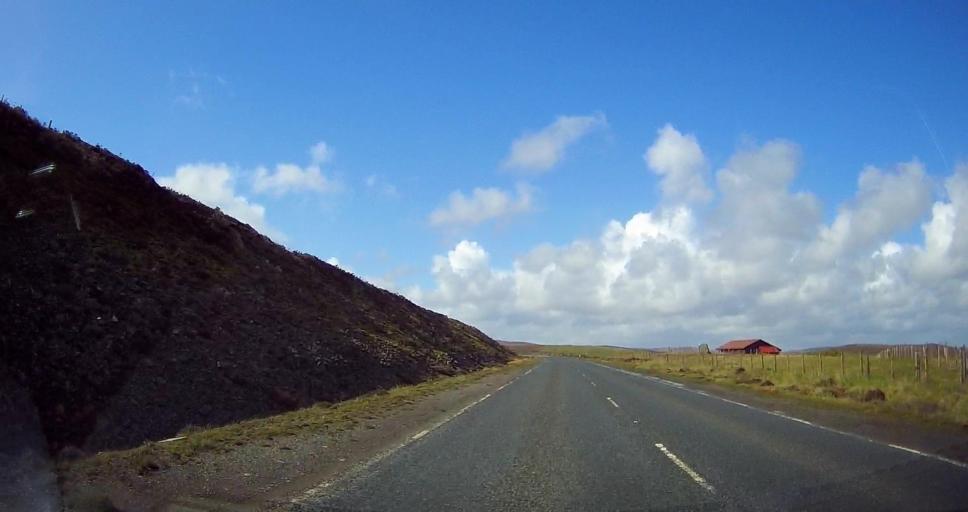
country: GB
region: Scotland
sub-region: Shetland Islands
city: Lerwick
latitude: 60.2212
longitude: -1.2342
